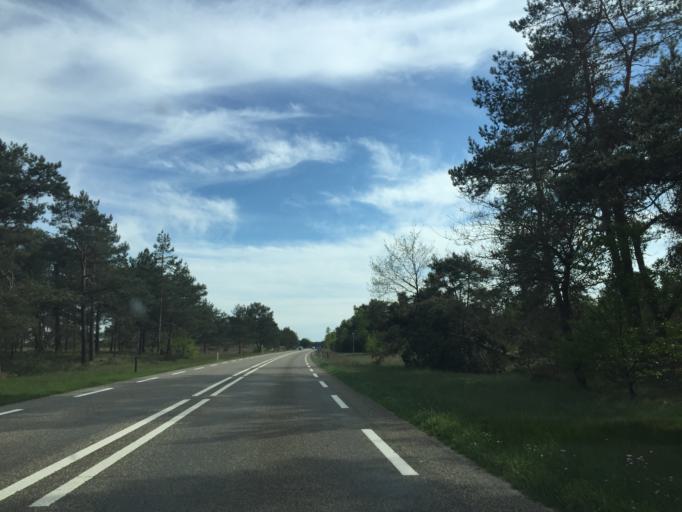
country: NL
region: Gelderland
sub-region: Gemeente Apeldoorn
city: Uddel
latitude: 52.2117
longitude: 5.7803
